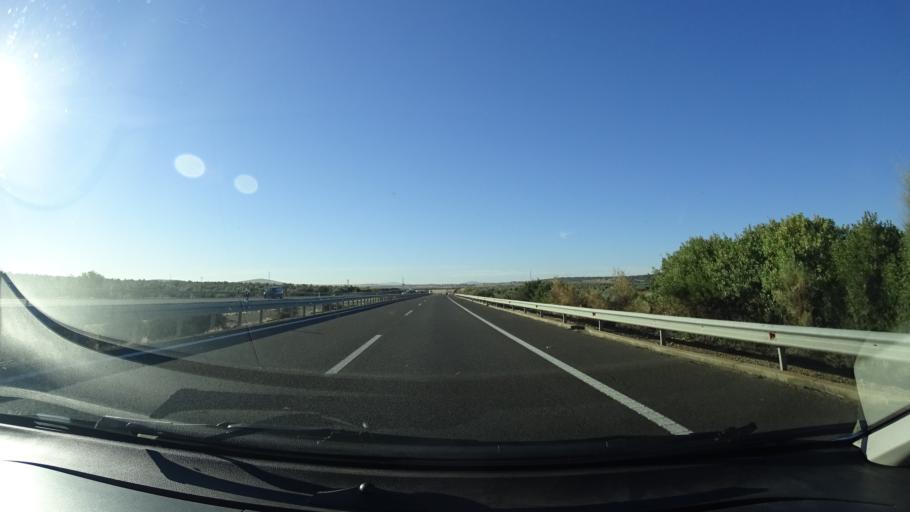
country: ES
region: Extremadura
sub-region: Provincia de Badajoz
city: Fuente de Cantos
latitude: 38.3348
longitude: -6.3126
